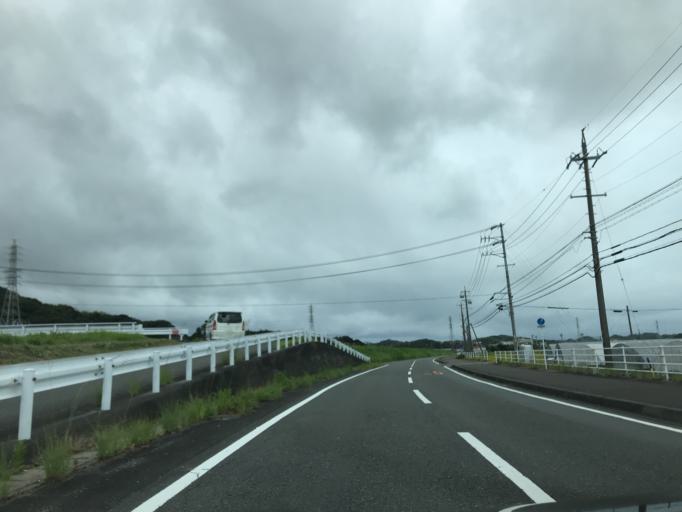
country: JP
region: Shizuoka
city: Sagara
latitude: 34.6597
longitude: 138.1373
